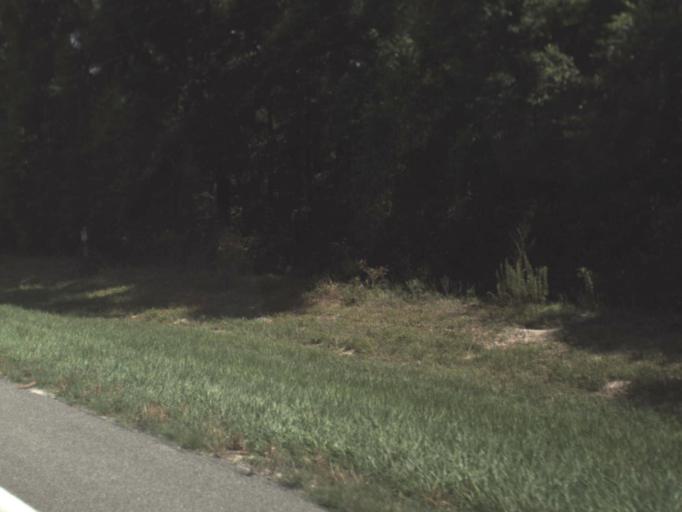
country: US
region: Florida
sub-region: Lafayette County
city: Mayo
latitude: 29.9679
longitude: -82.9779
